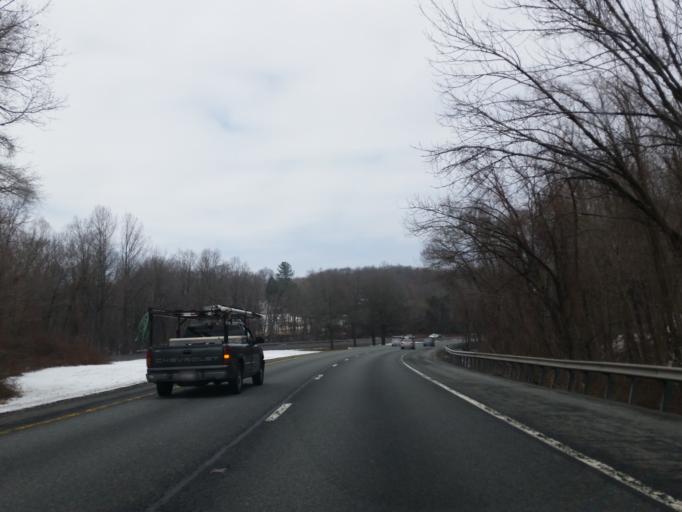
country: US
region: Maryland
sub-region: Baltimore County
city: Hunt Valley
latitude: 39.5765
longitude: -76.6758
